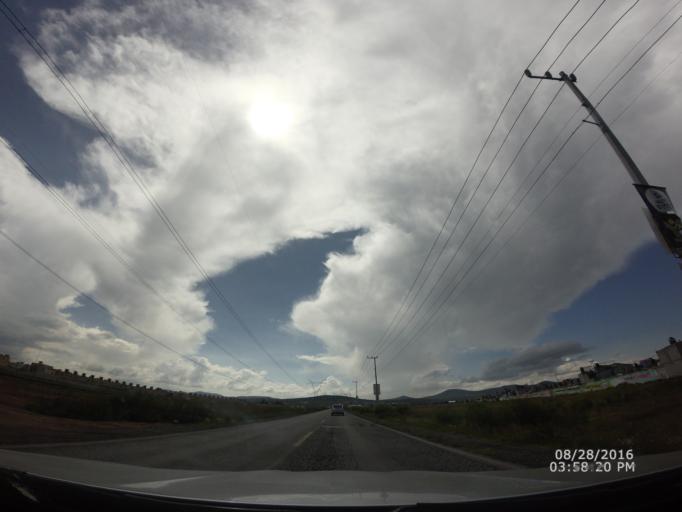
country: MX
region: Hidalgo
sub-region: Mineral de la Reforma
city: La Colonia
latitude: 20.0364
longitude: -98.7783
